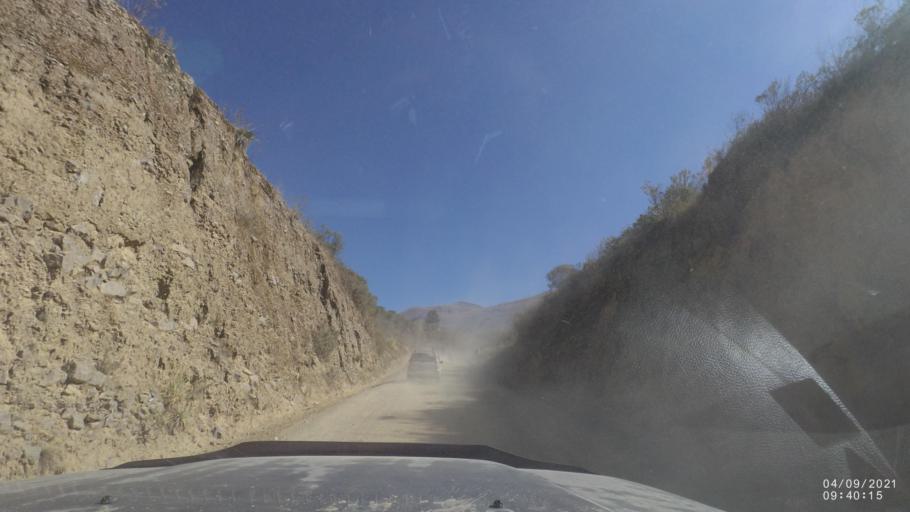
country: BO
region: Cochabamba
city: Sipe Sipe
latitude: -17.3431
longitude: -66.3868
